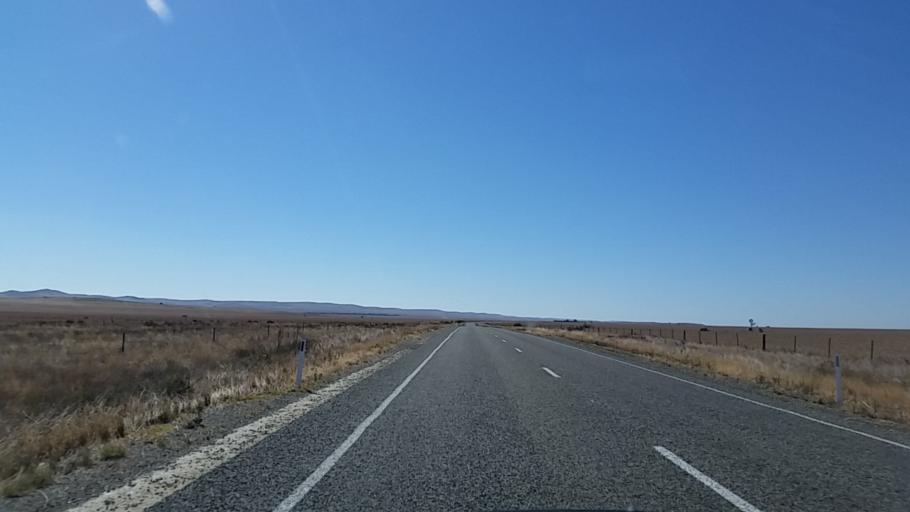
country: AU
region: South Australia
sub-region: Northern Areas
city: Jamestown
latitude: -33.2782
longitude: 138.8687
